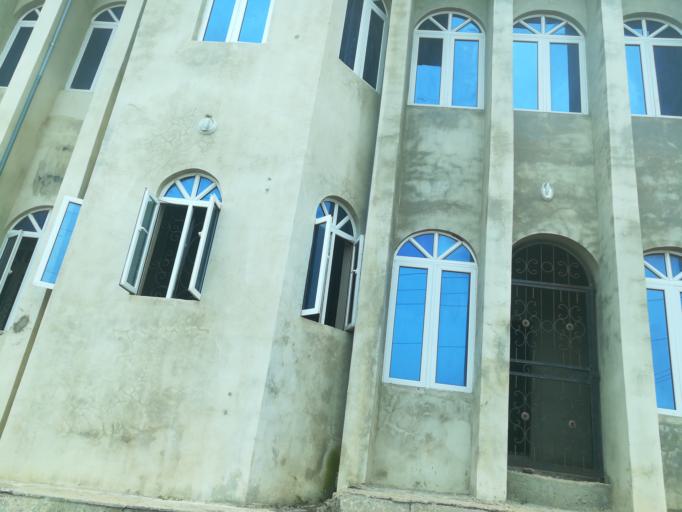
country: NG
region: Lagos
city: Ikorodu
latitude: 6.5641
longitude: 3.5903
